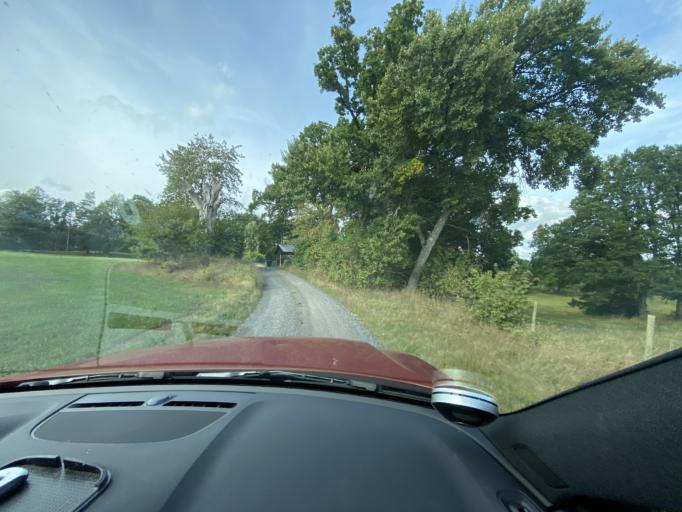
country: SE
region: Skane
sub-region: Hassleholms Kommun
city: Hastveda
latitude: 56.3567
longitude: 13.8805
